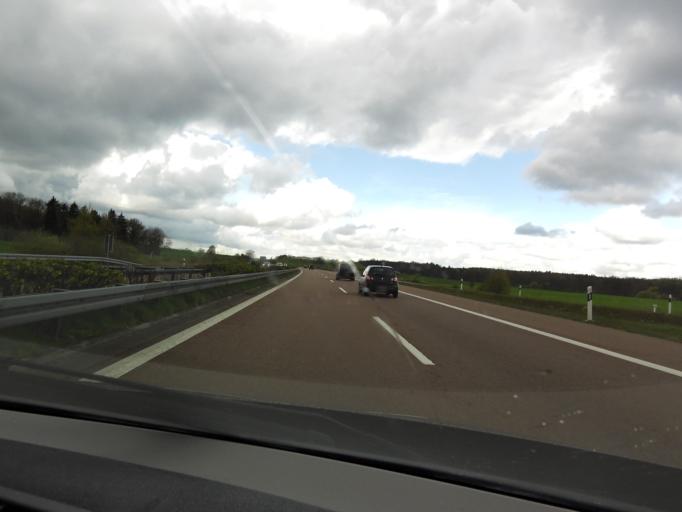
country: DE
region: Mecklenburg-Vorpommern
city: Tessin
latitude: 54.0318
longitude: 12.4066
